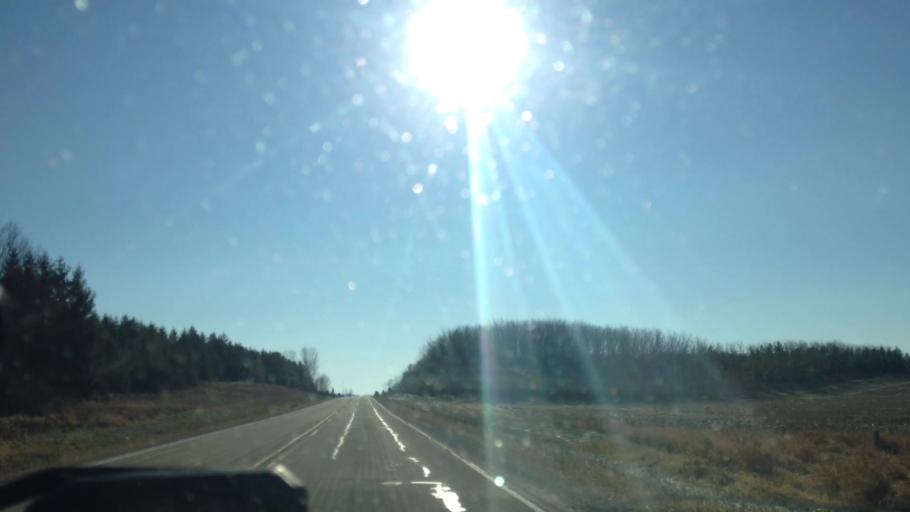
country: US
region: Wisconsin
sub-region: Dodge County
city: Mayville
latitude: 43.4909
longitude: -88.5189
